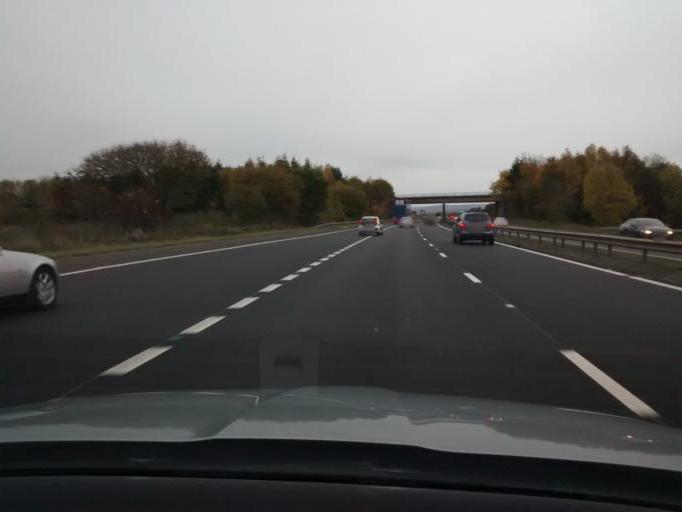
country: GB
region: Scotland
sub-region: Falkirk
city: Airth
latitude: 56.0421
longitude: -3.7793
